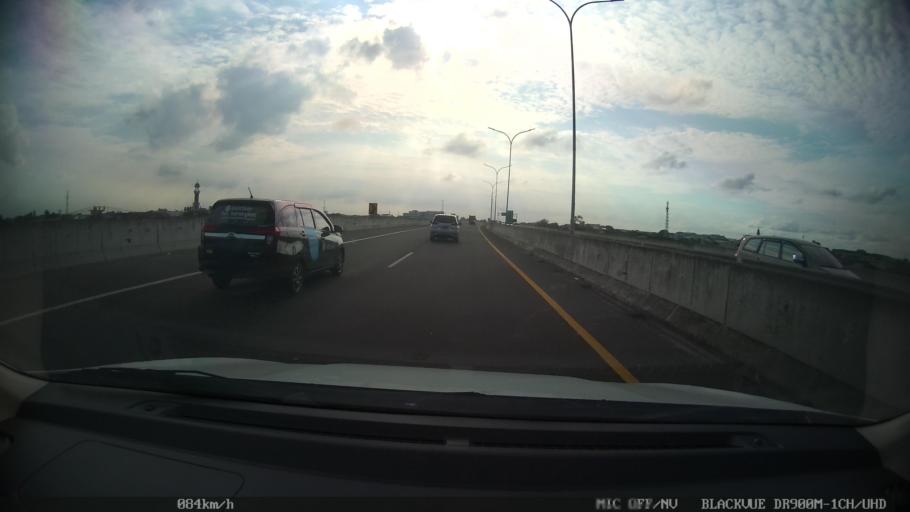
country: ID
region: North Sumatra
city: Medan
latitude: 3.6475
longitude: 98.6707
